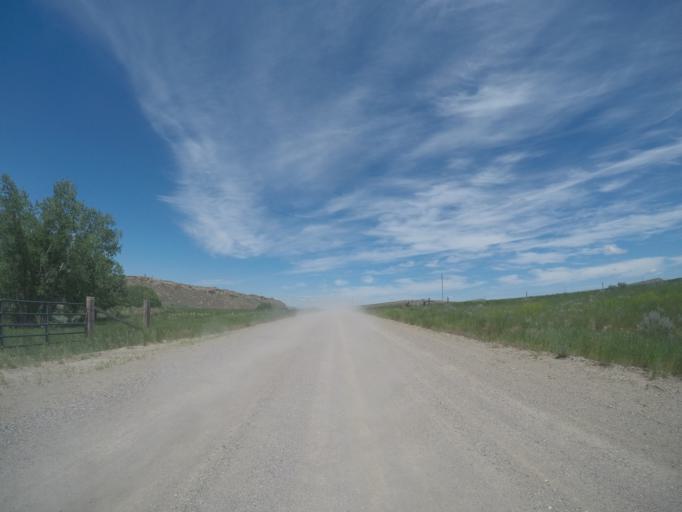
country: US
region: Montana
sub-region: Carbon County
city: Red Lodge
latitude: 45.2341
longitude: -108.8521
